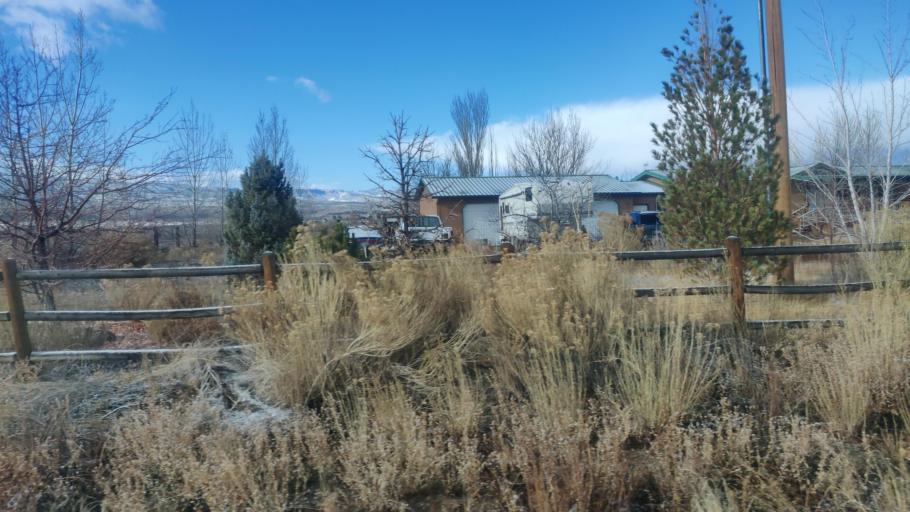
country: US
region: Colorado
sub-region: Mesa County
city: Clifton
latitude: 38.9926
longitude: -108.4249
